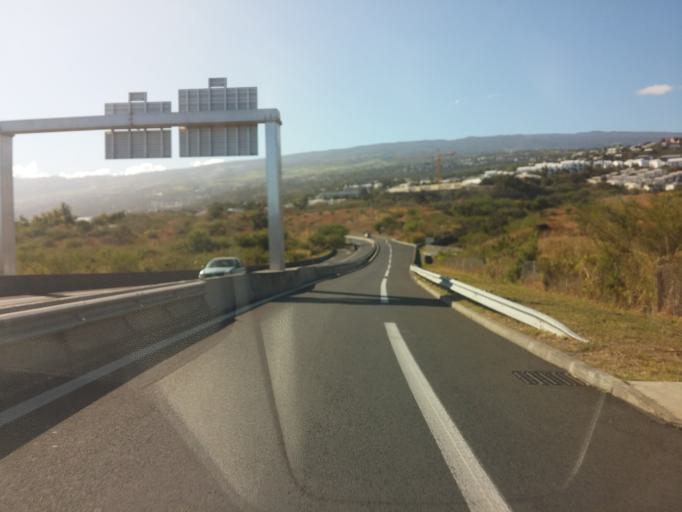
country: RE
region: Reunion
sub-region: Reunion
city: Saint-Paul
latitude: -21.0195
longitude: 55.2596
